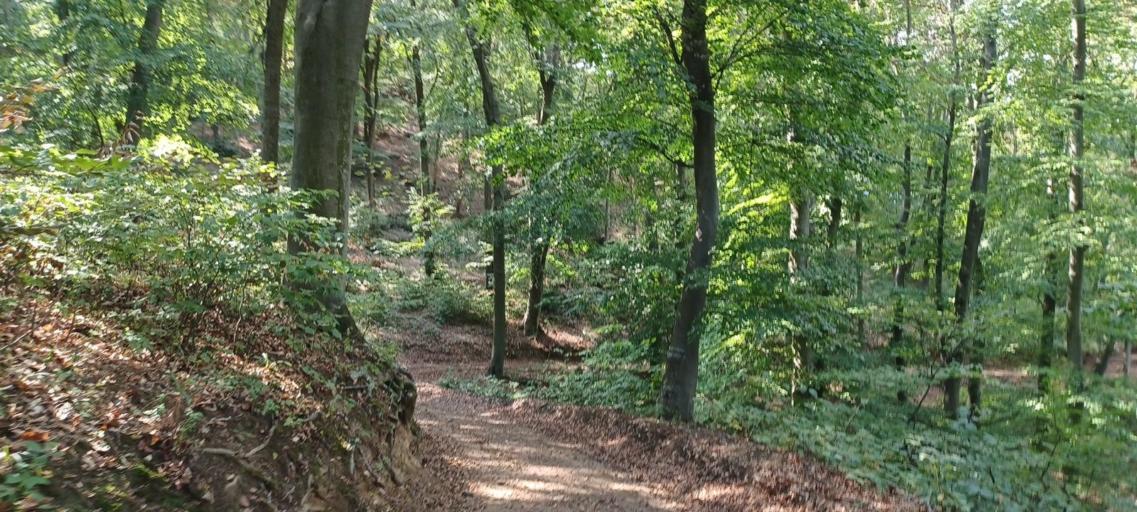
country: HU
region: Tolna
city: Szentgalpuszta
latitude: 46.3275
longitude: 18.6243
